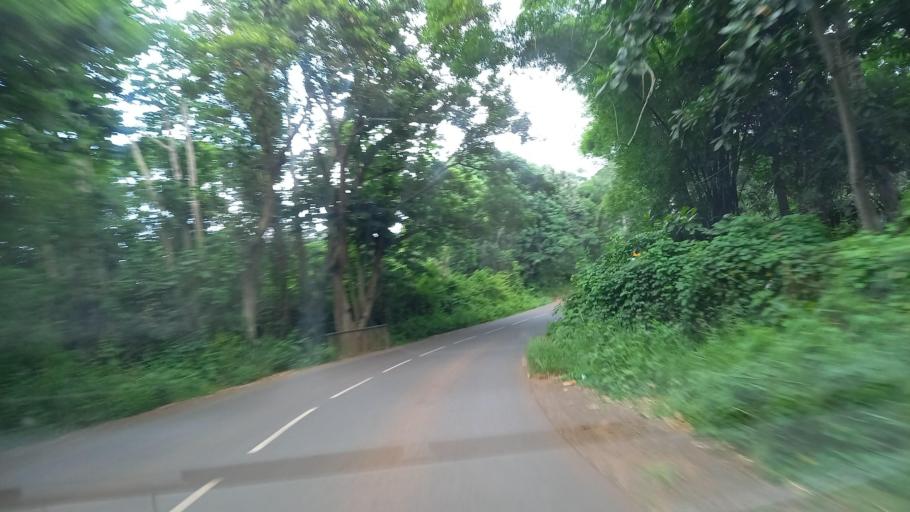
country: YT
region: Ouangani
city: Ouangani
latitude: -12.8331
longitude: 45.1390
